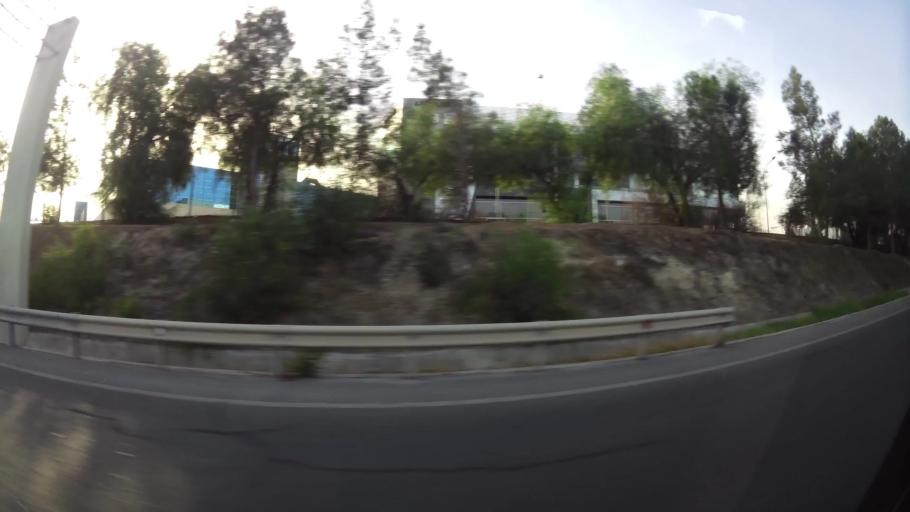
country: CY
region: Lefkosia
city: Nicosia
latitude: 35.1306
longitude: 33.3695
